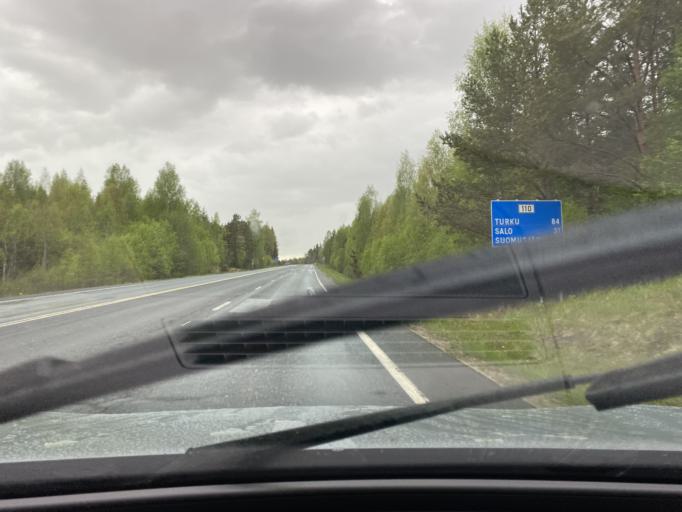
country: FI
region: Varsinais-Suomi
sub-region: Salo
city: Suomusjaervi
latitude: 60.3702
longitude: 23.6752
